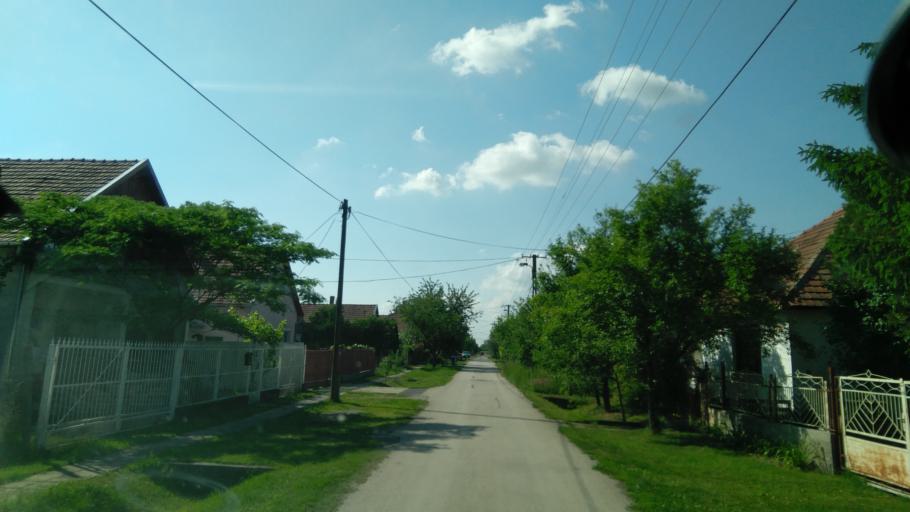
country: HU
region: Bekes
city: Doboz
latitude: 46.6997
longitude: 21.1890
